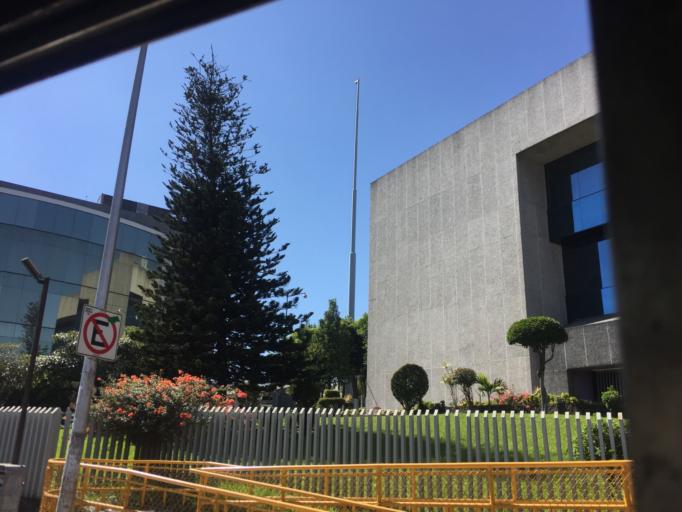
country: MX
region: Veracruz
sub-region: Xalapa
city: Xalapa de Enriquez
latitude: 19.5388
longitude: -96.9079
